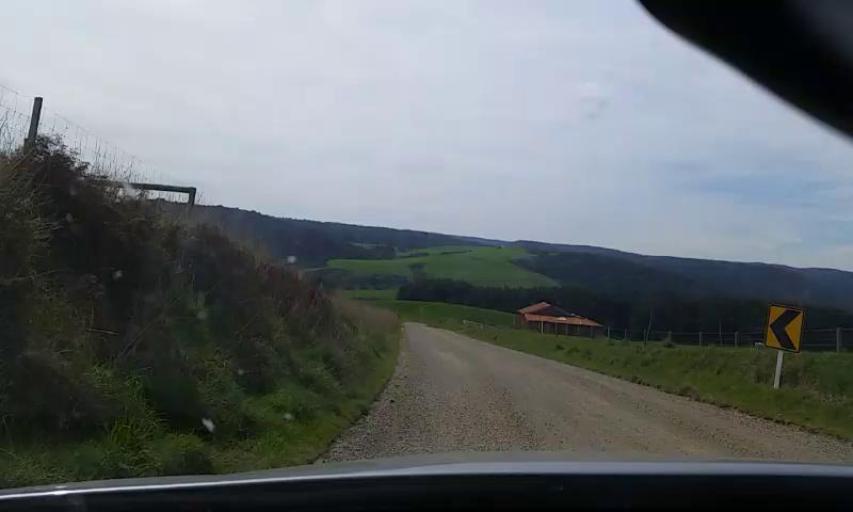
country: NZ
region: Otago
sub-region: Clutha District
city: Papatowai
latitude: -46.6304
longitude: 168.9824
